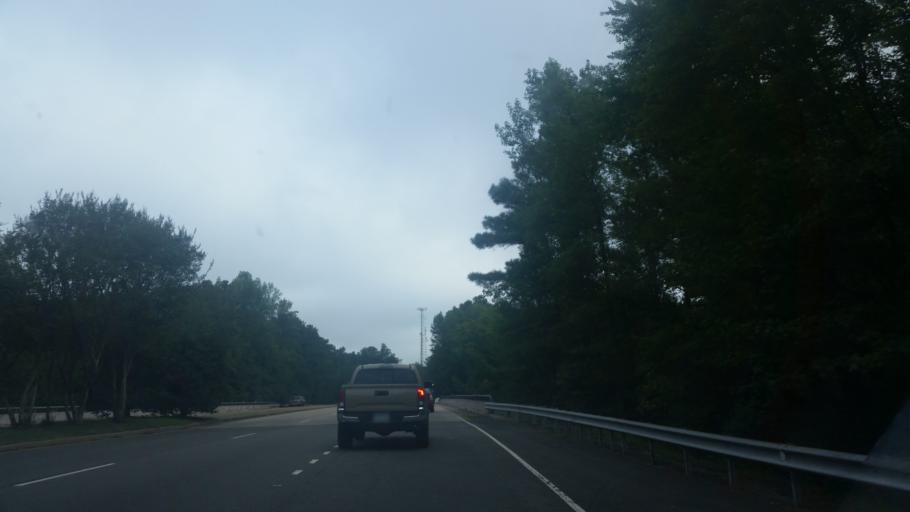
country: US
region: Virginia
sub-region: Henrico County
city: Sandston
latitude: 37.5154
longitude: -77.1899
